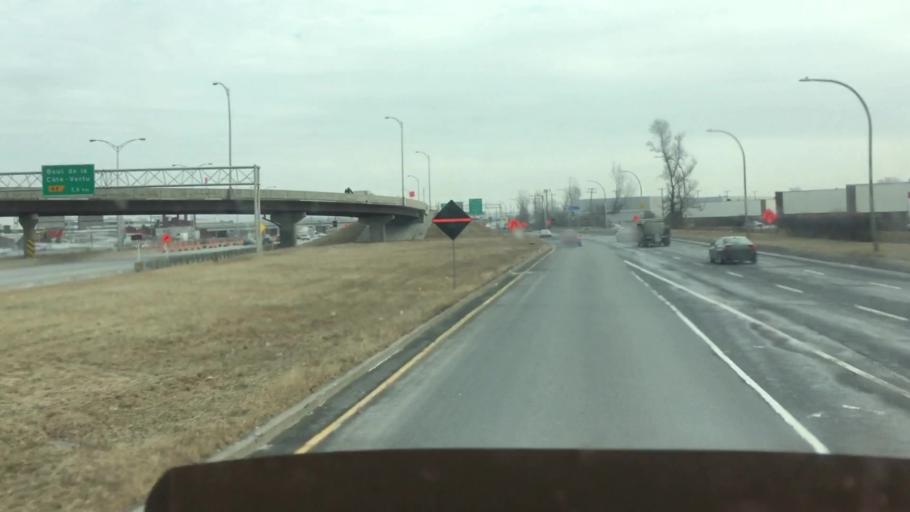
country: CA
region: Quebec
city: Dorval
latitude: 45.4902
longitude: -73.7423
